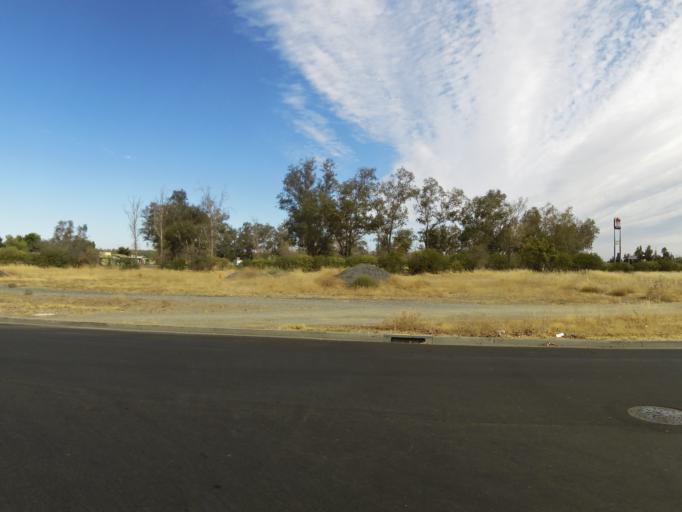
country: US
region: California
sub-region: Glenn County
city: Orland
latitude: 39.7524
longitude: -122.2081
